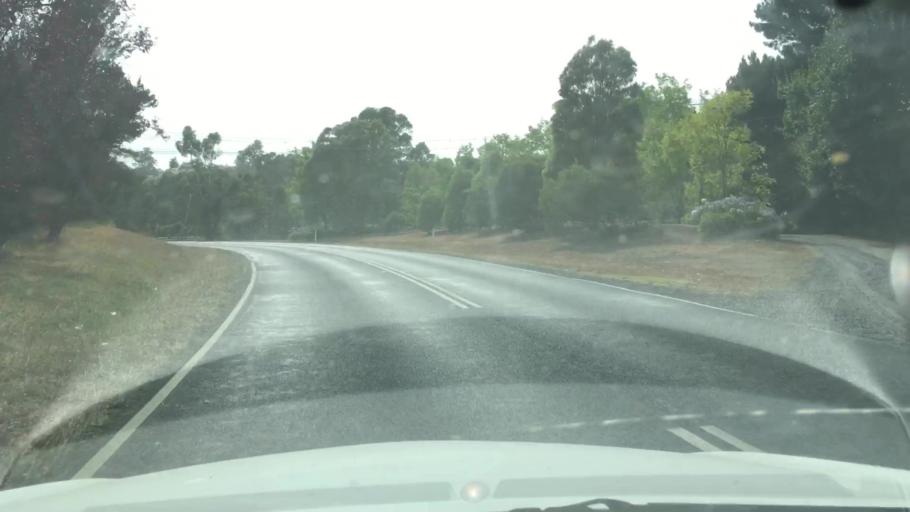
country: AU
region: Victoria
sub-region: Yarra Ranges
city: Woori Yallock
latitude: -37.8061
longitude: 145.5211
